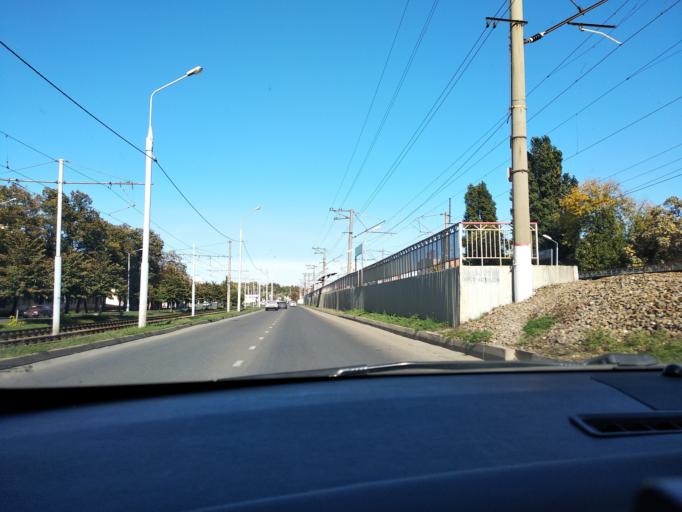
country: RU
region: Adygeya
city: Yablonovskiy
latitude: 45.0042
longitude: 38.9660
